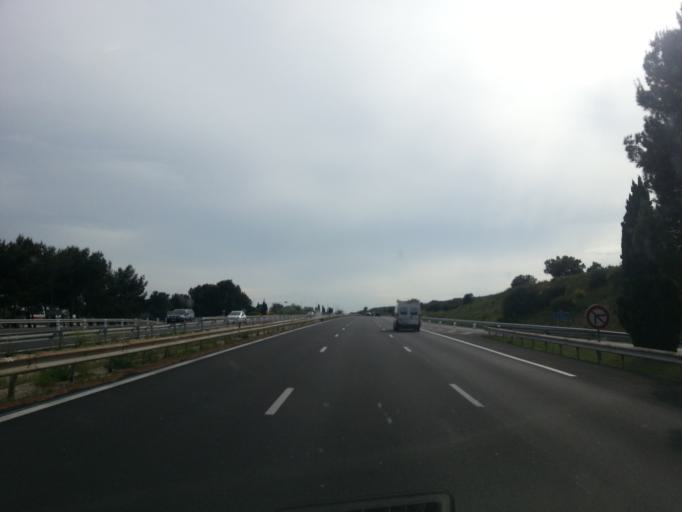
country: FR
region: Languedoc-Roussillon
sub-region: Departement du Gard
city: Tavel
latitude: 44.0012
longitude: 4.7020
